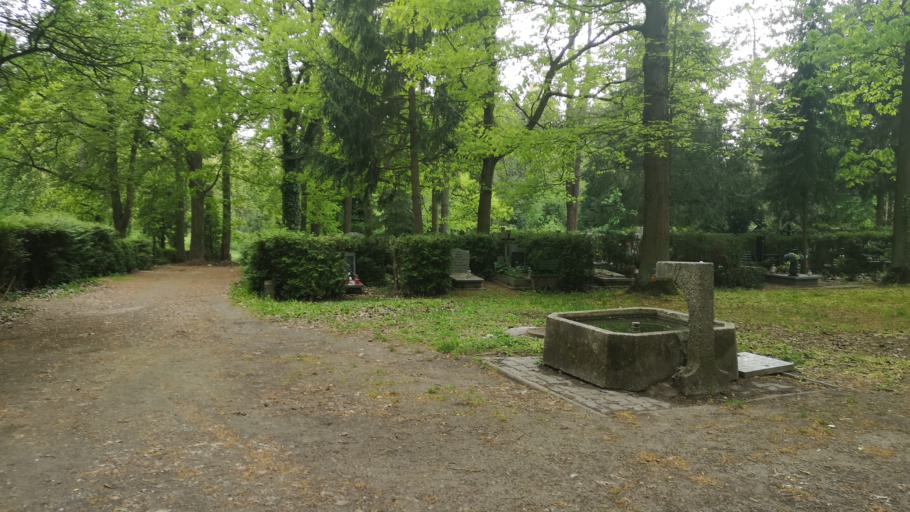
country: PL
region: West Pomeranian Voivodeship
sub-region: Szczecin
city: Szczecin
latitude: 53.4139
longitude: 14.5114
